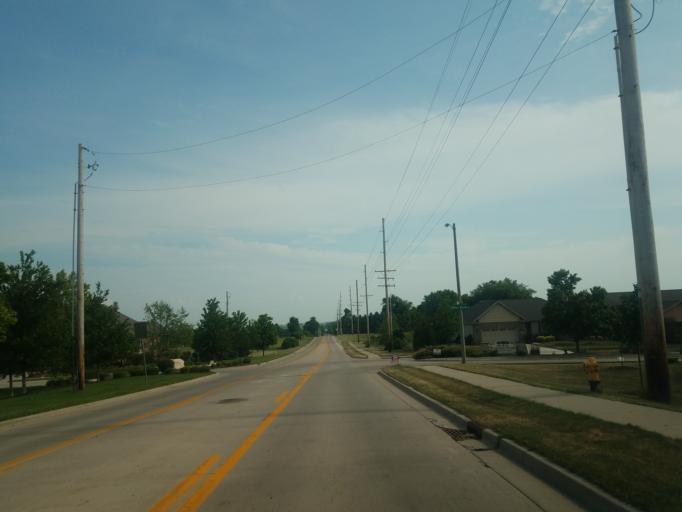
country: US
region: Illinois
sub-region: McLean County
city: Bloomington
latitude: 40.4481
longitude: -89.0057
